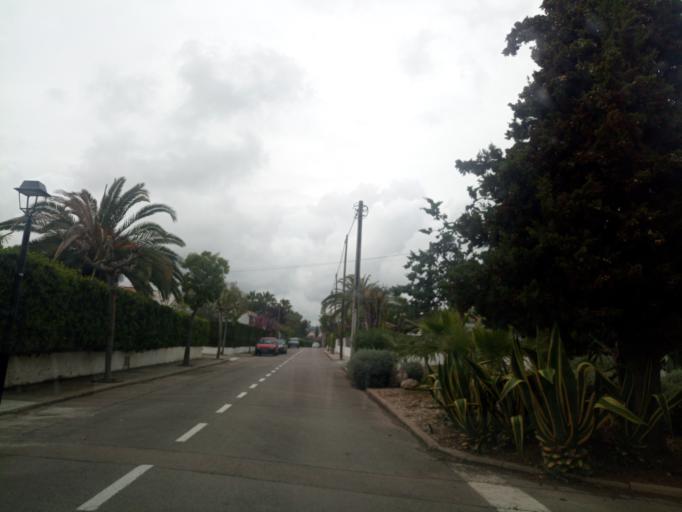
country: ES
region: Catalonia
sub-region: Provincia de Barcelona
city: Sant Pere de Ribes
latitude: 41.2533
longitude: 1.7791
